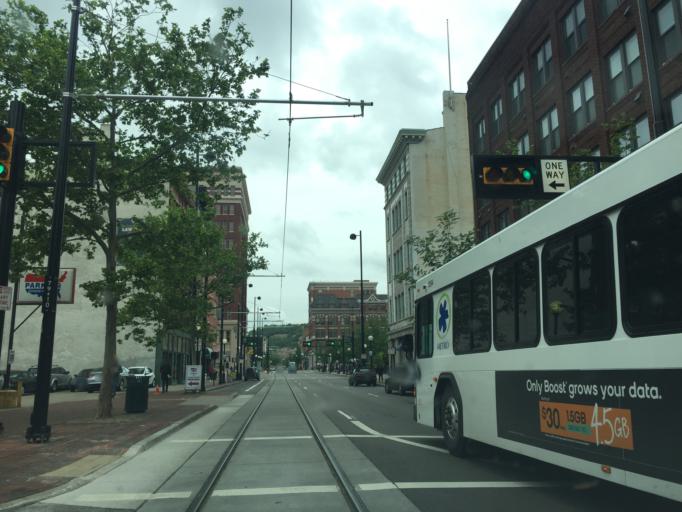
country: US
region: Kentucky
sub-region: Campbell County
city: Newport
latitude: 39.1059
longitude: -84.5108
